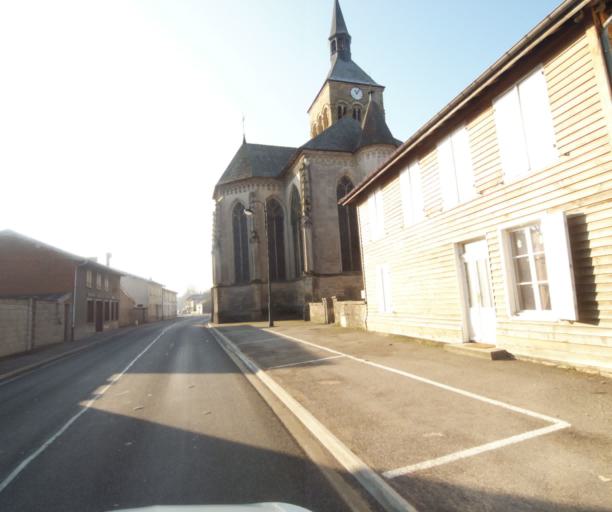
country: FR
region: Champagne-Ardenne
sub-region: Departement de la Haute-Marne
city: Montier-en-Der
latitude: 48.4716
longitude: 4.7644
